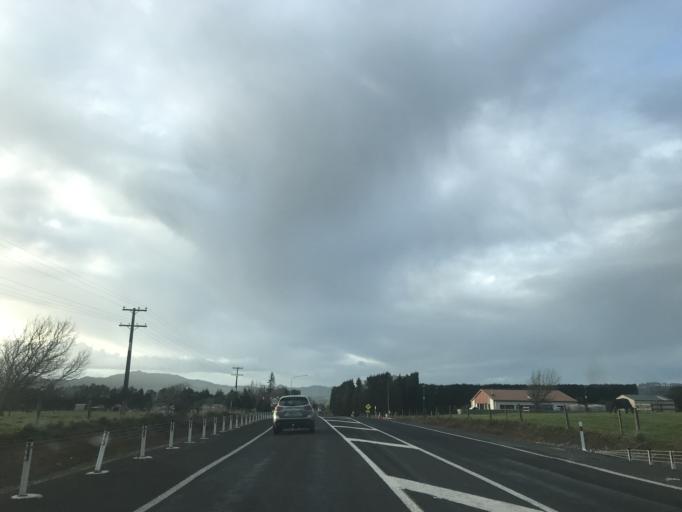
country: NZ
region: Waikato
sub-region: Hauraki District
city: Waihi
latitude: -37.4309
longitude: 175.8717
